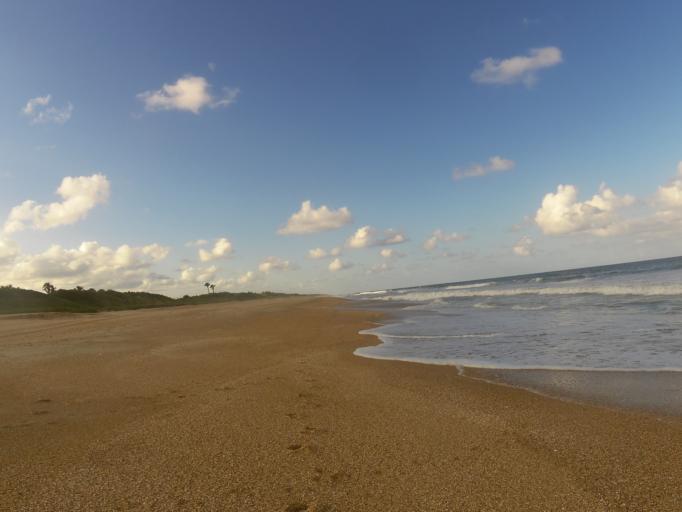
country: US
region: Florida
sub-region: Saint Johns County
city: Palm Valley
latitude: 30.0952
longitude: -81.3394
